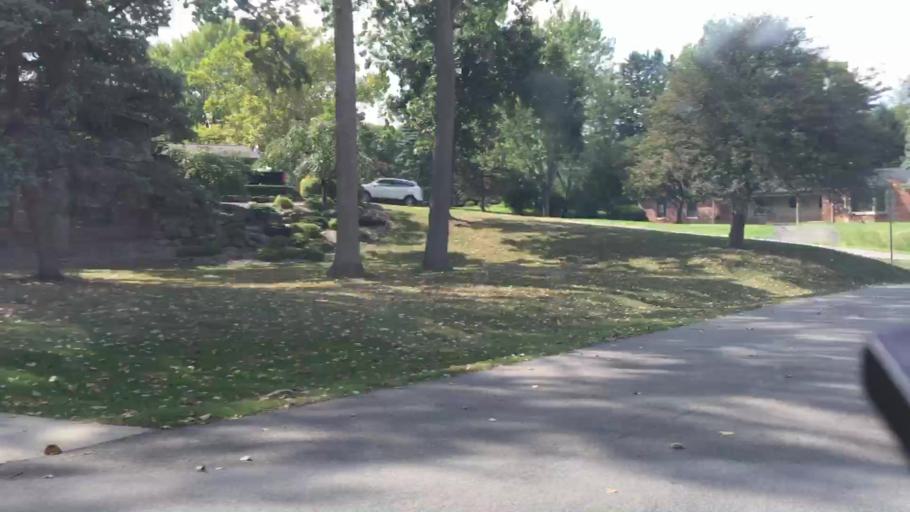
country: US
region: Michigan
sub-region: Oakland County
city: Sylvan Lake
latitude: 42.5716
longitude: -83.3095
